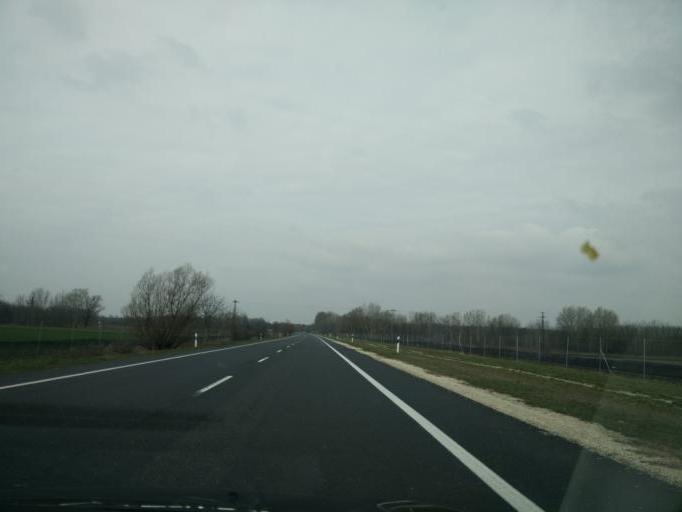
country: HU
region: Gyor-Moson-Sopron
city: Toltestava
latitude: 47.7051
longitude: 17.7596
